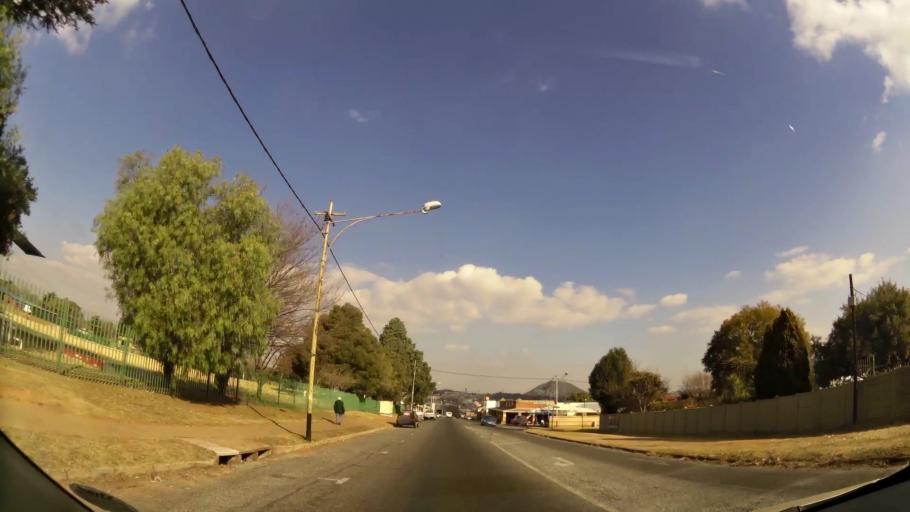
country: ZA
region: Gauteng
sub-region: West Rand District Municipality
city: Krugersdorp
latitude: -26.0901
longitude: 27.7685
